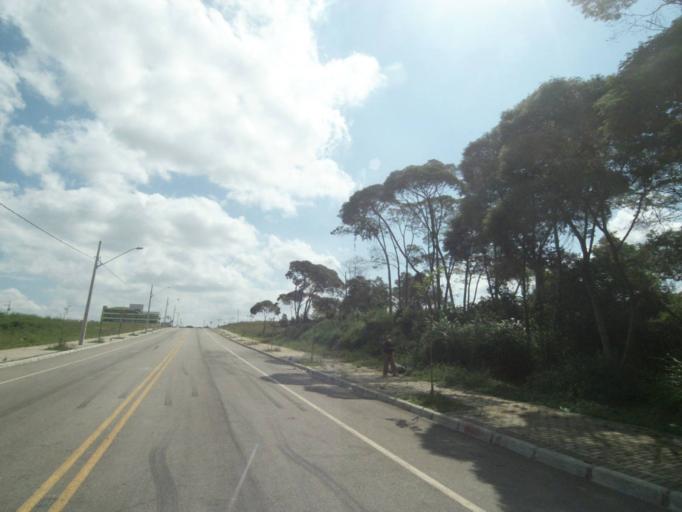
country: BR
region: Parana
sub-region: Curitiba
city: Curitiba
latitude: -25.5072
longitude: -49.3071
